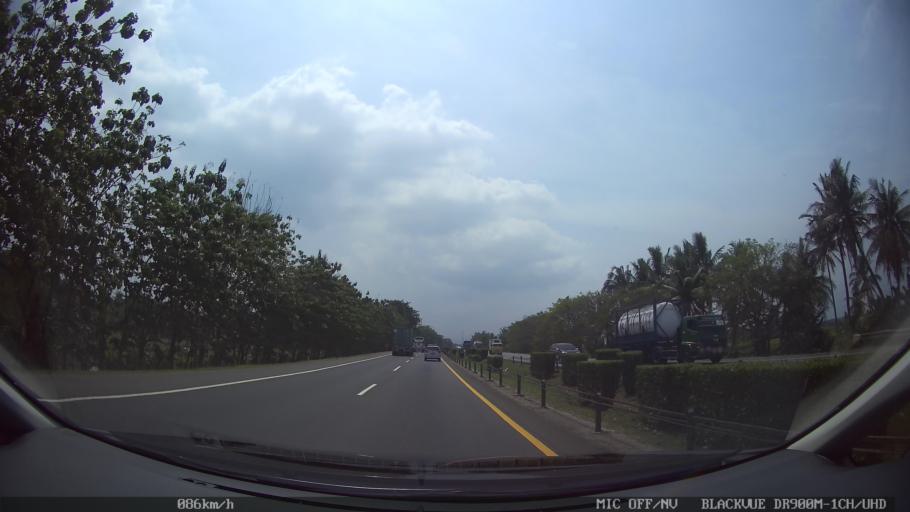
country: ID
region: Banten
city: Bojonegara
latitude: -6.0435
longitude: 106.1085
